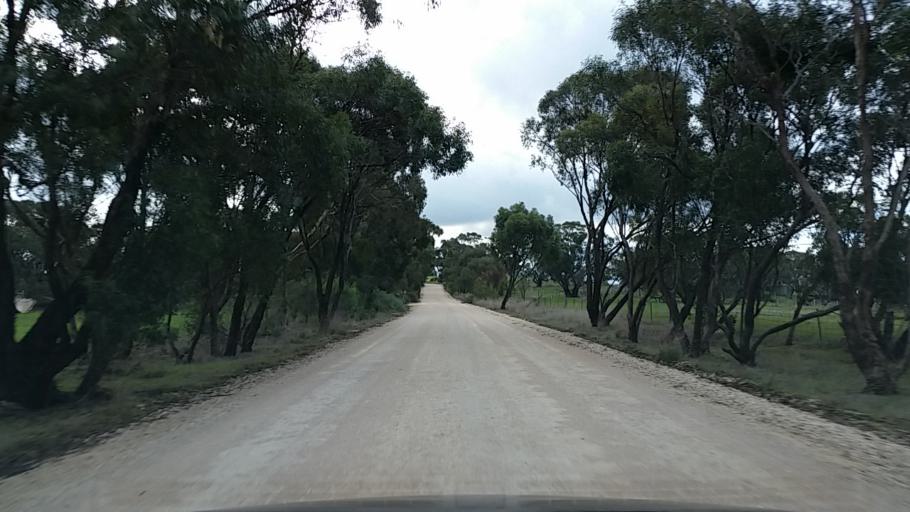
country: AU
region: South Australia
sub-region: Mount Barker
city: Callington
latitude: -34.9995
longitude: 139.0597
